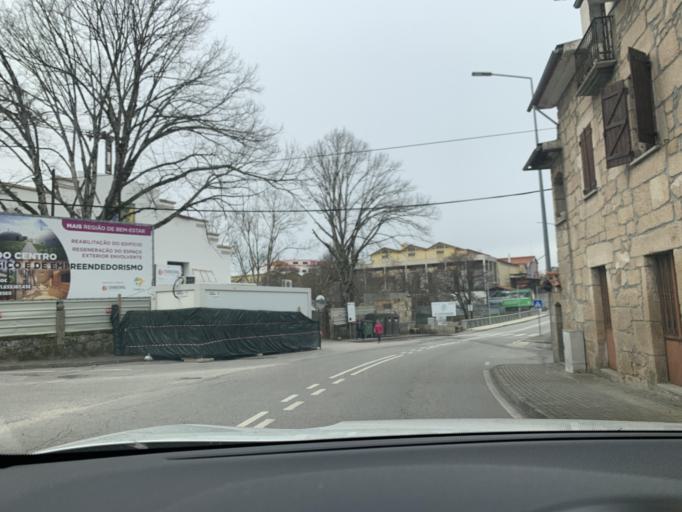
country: PT
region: Viseu
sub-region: Concelho de Tondela
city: Tondela
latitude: 40.5233
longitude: -8.0704
